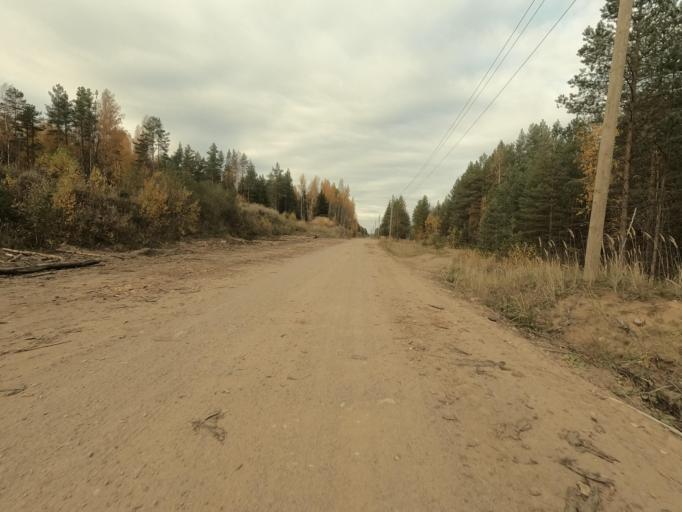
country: RU
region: Leningrad
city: Priladozhskiy
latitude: 59.6917
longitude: 31.3610
